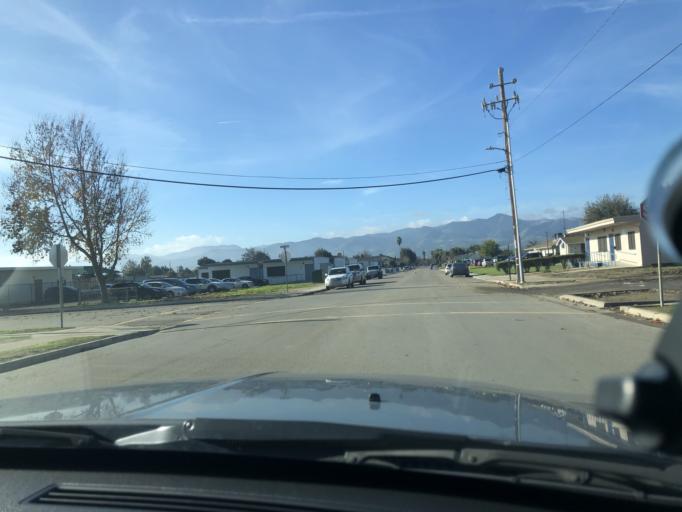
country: US
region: California
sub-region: Monterey County
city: King City
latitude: 36.2166
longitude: -121.1329
